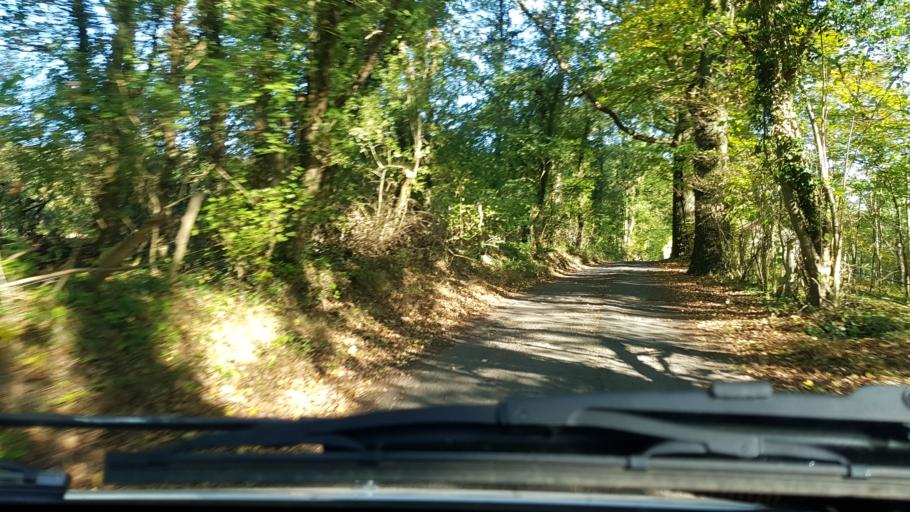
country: GB
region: England
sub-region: Surrey
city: Ockley
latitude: 51.1322
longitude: -0.3493
